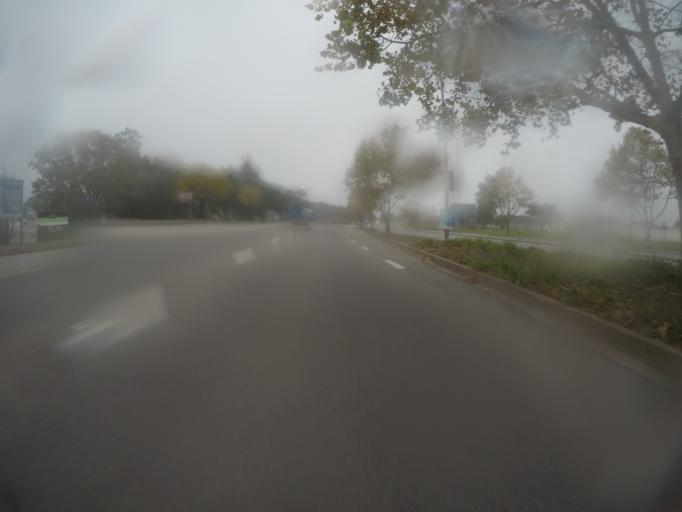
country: ZA
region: Western Cape
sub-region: Eden District Municipality
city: George
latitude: -33.9786
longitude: 22.4414
